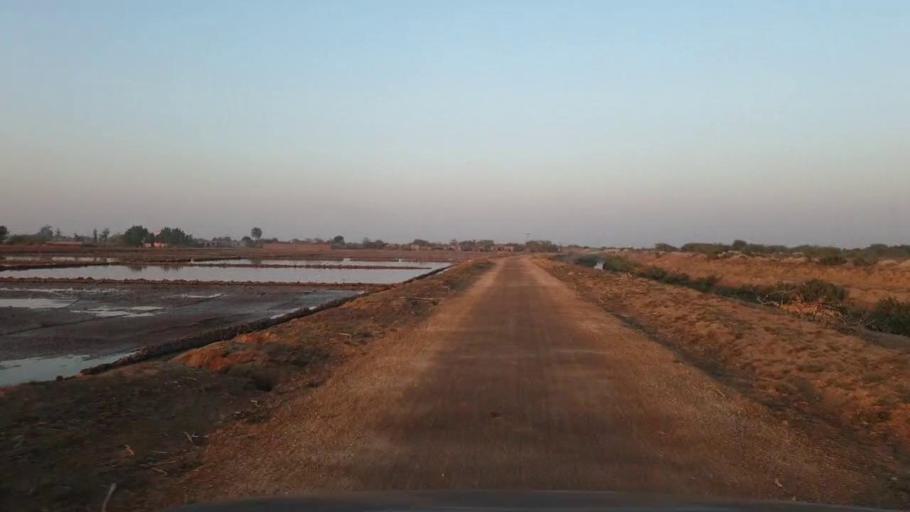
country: PK
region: Sindh
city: Digri
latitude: 25.1399
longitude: 69.2537
